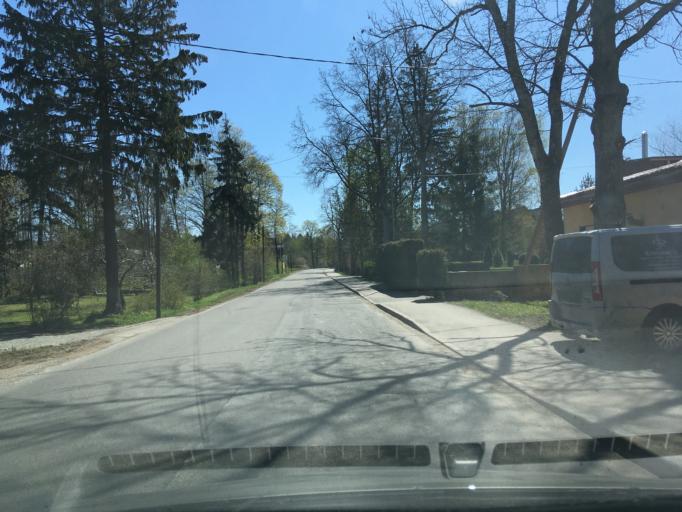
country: EE
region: Harju
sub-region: Raasiku vald
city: Arukula
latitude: 59.3677
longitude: 25.0804
